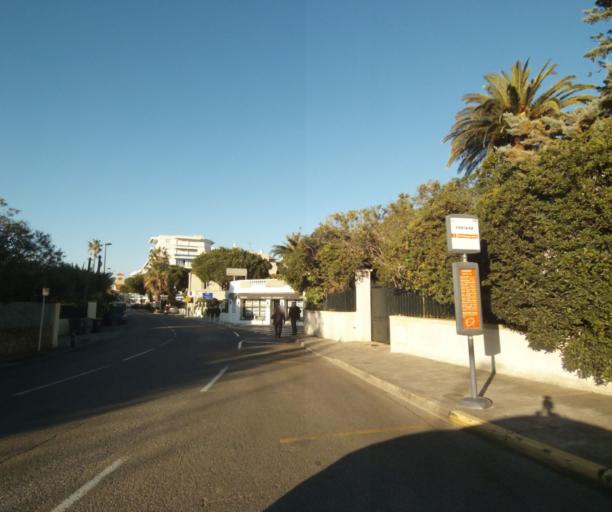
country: FR
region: Provence-Alpes-Cote d'Azur
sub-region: Departement des Alpes-Maritimes
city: Antibes
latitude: 43.5518
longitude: 7.1288
